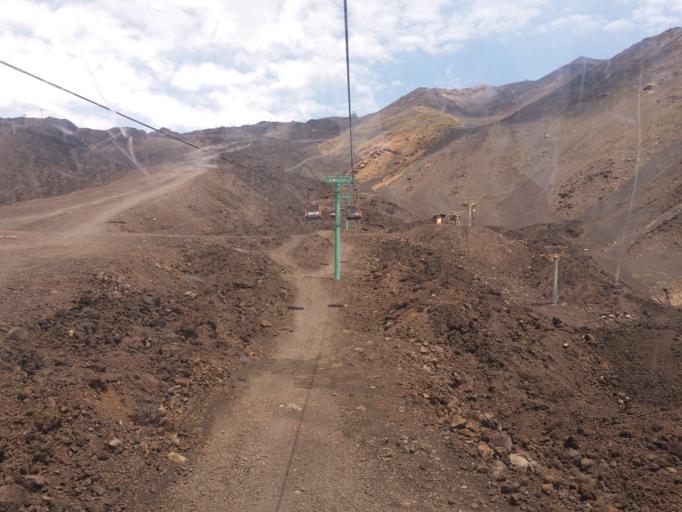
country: IT
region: Sicily
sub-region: Catania
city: Ragalna
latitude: 37.7069
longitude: 14.9993
